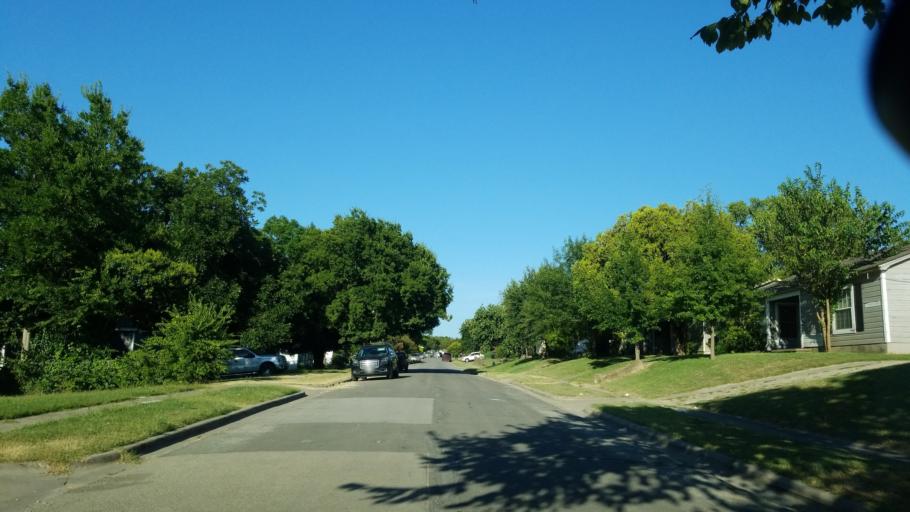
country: US
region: Texas
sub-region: Dallas County
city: Dallas
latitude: 32.7783
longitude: -96.7143
